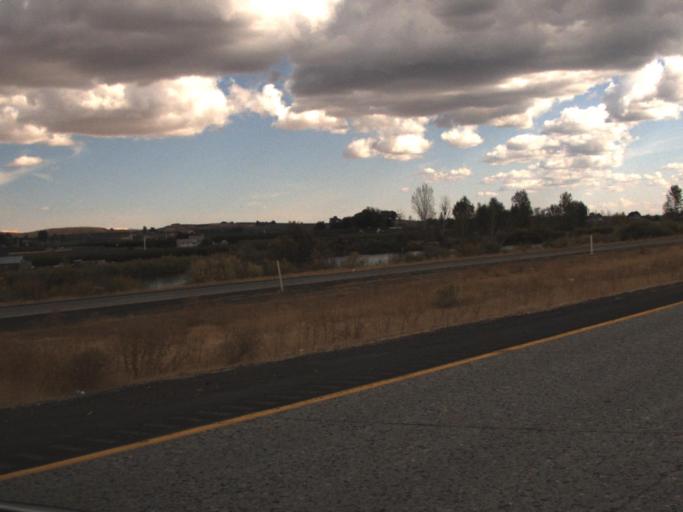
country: US
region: Washington
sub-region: Yakima County
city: Wapato
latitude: 46.4831
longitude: -120.4104
